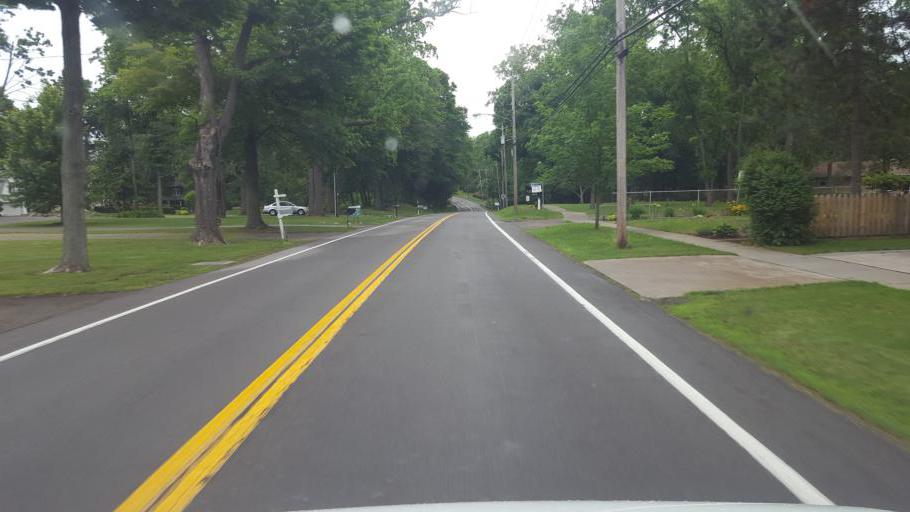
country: US
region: New York
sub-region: Niagara County
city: Youngstown
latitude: 43.2407
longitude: -79.0512
